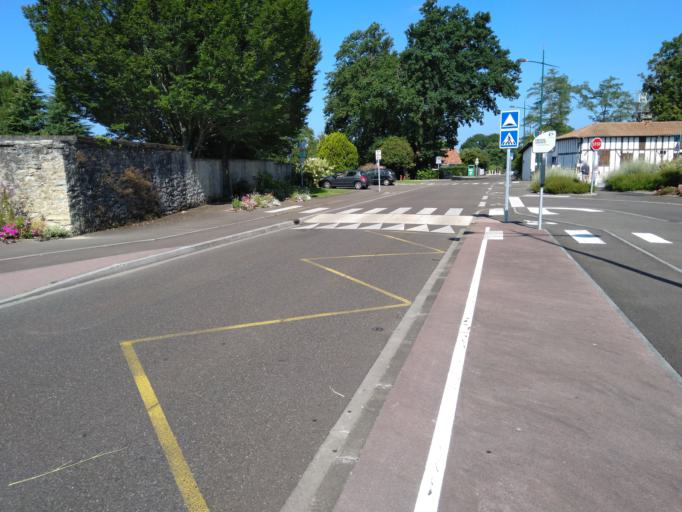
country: FR
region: Aquitaine
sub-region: Departement des Landes
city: Saint-Paul-les-Dax
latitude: 43.7273
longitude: -1.0600
